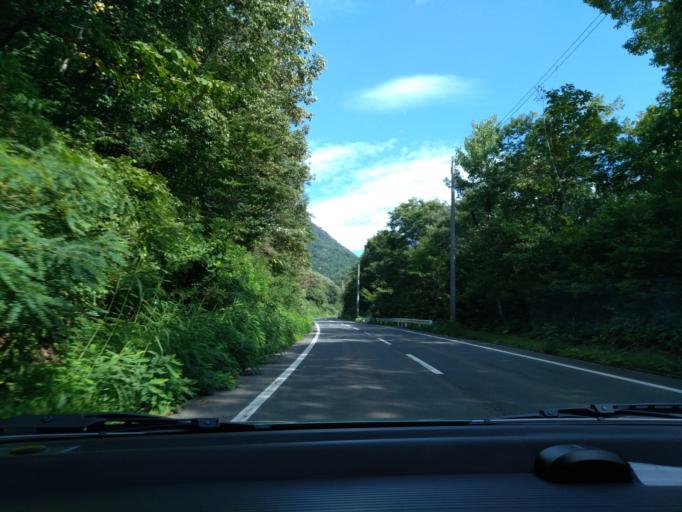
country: JP
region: Iwate
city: Shizukuishi
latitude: 39.6376
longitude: 141.0231
